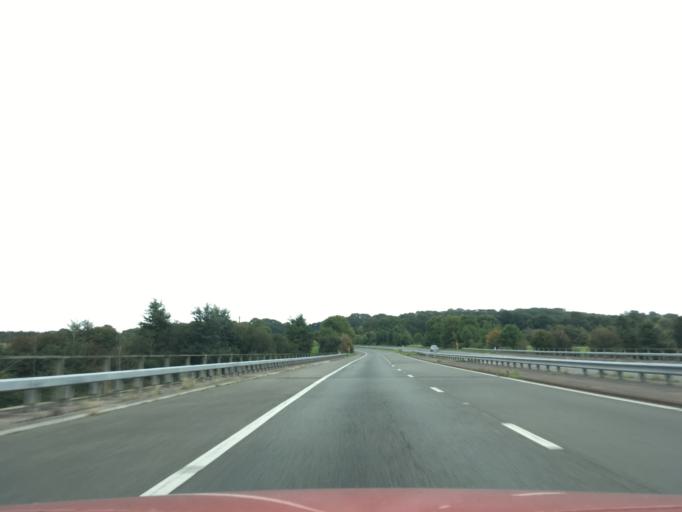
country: GB
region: Wales
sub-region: Monmouthshire
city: Caldicot
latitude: 51.6031
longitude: -2.7491
